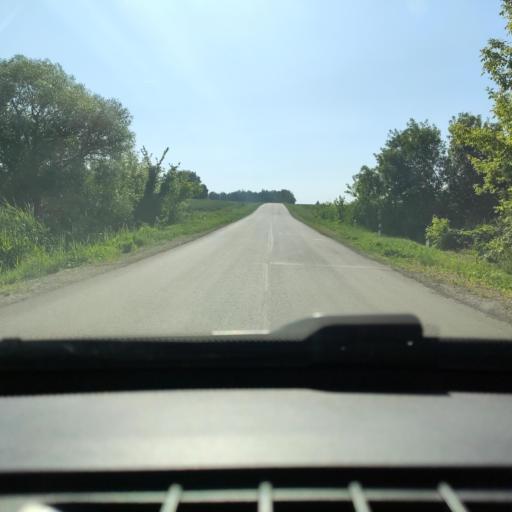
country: RU
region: Voronezj
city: Pereleshinskiy
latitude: 51.6450
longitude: 40.3011
